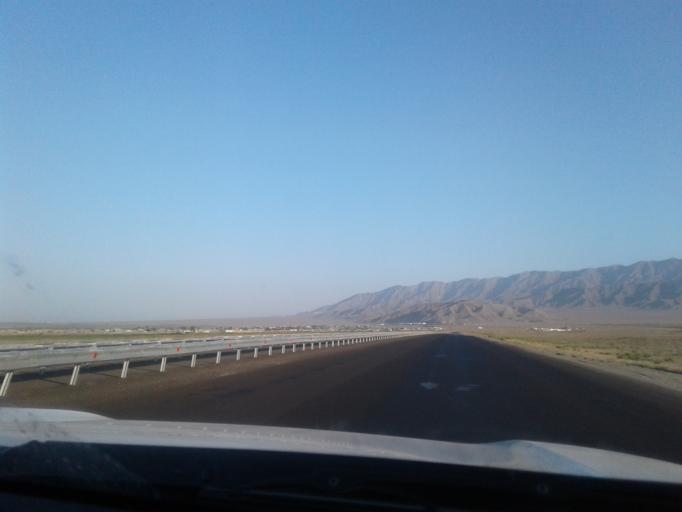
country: TM
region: Ahal
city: Baharly
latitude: 38.5570
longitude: 57.1374
